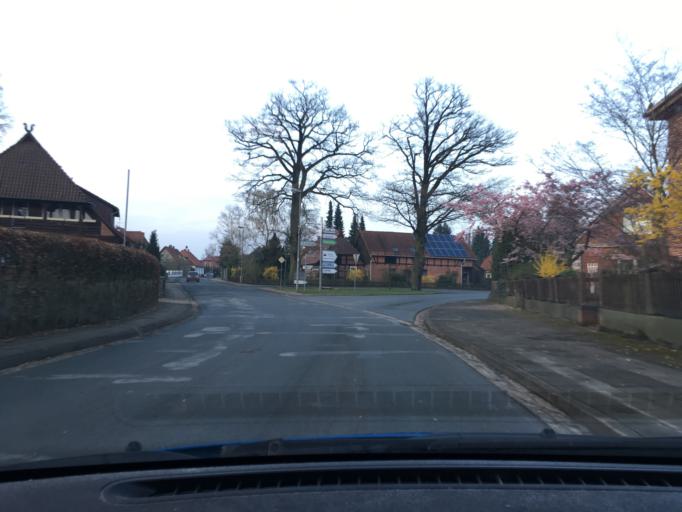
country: DE
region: Lower Saxony
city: Bad Fallingbostel
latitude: 52.8973
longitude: 9.7655
